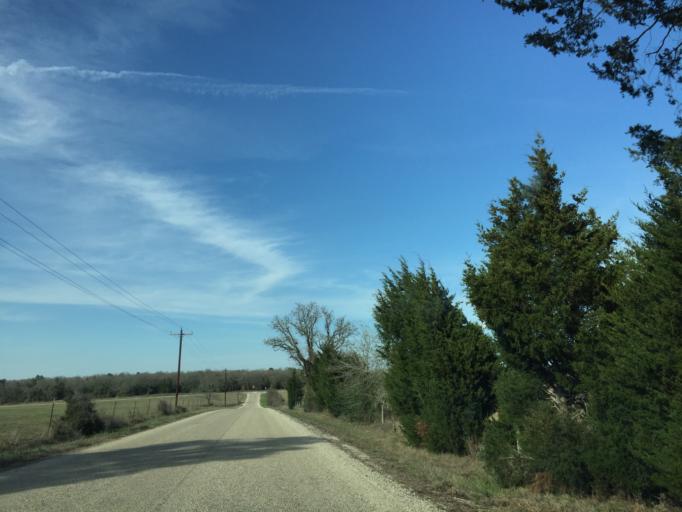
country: US
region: Texas
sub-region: Milam County
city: Thorndale
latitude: 30.4567
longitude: -97.1916
